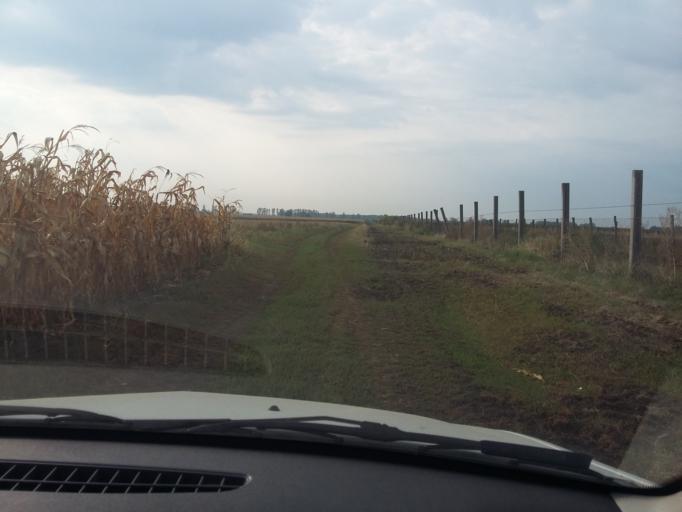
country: HU
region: Borsod-Abauj-Zemplen
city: Taktaharkany
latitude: 48.1327
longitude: 21.1068
